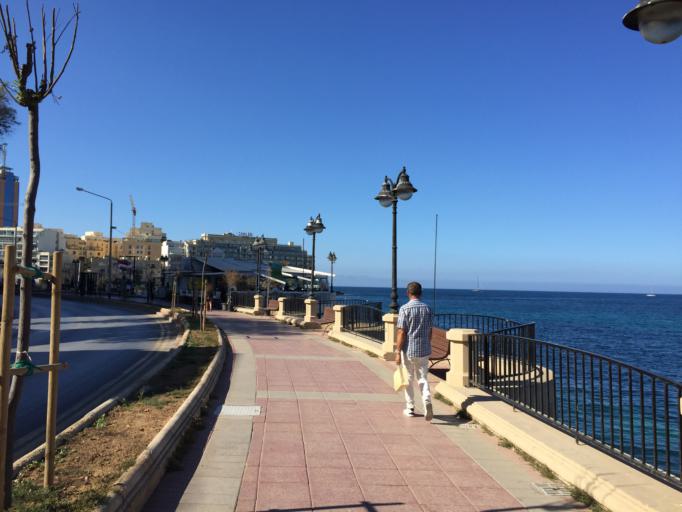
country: MT
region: Saint Julian
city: San Giljan
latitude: 35.9162
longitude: 14.4938
